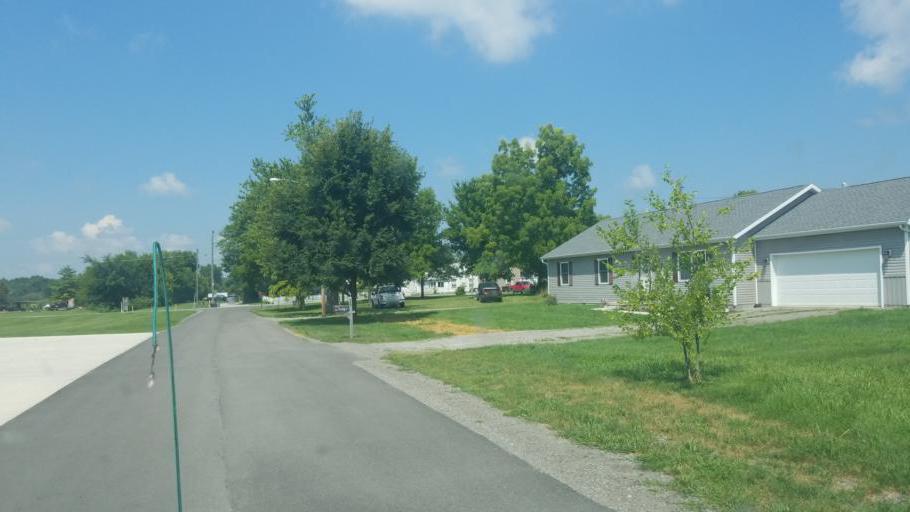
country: US
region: Ohio
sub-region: Hardin County
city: Ada
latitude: 40.7098
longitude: -83.9211
